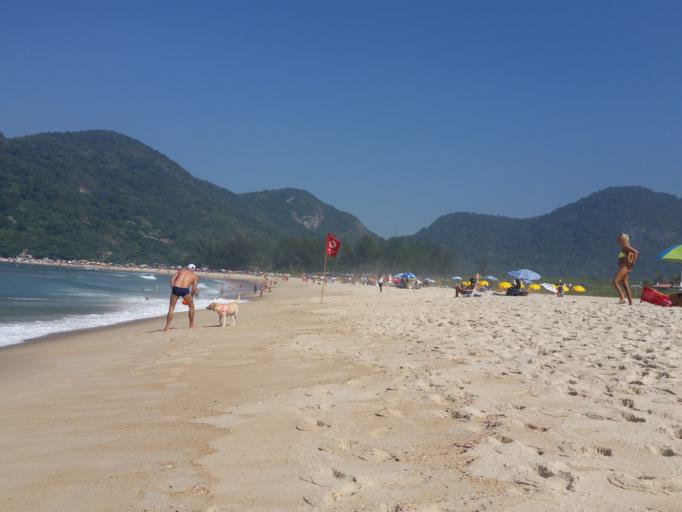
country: BR
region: Rio de Janeiro
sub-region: Nilopolis
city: Nilopolis
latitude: -23.0499
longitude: -43.5320
